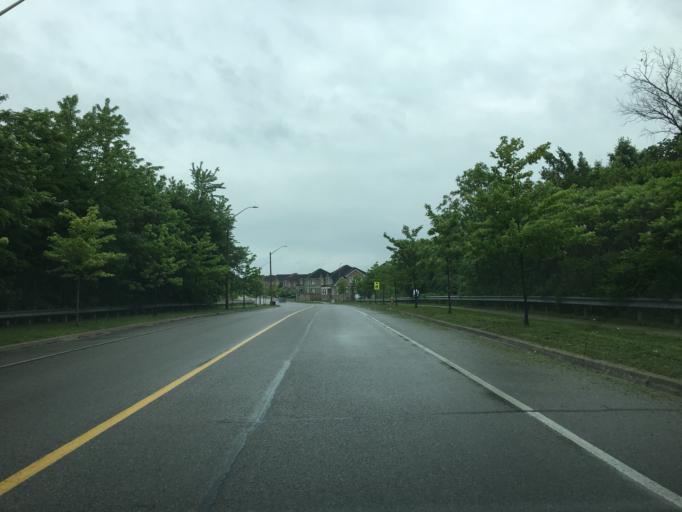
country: CA
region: Ontario
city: Markham
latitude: 43.8402
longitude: -79.2465
